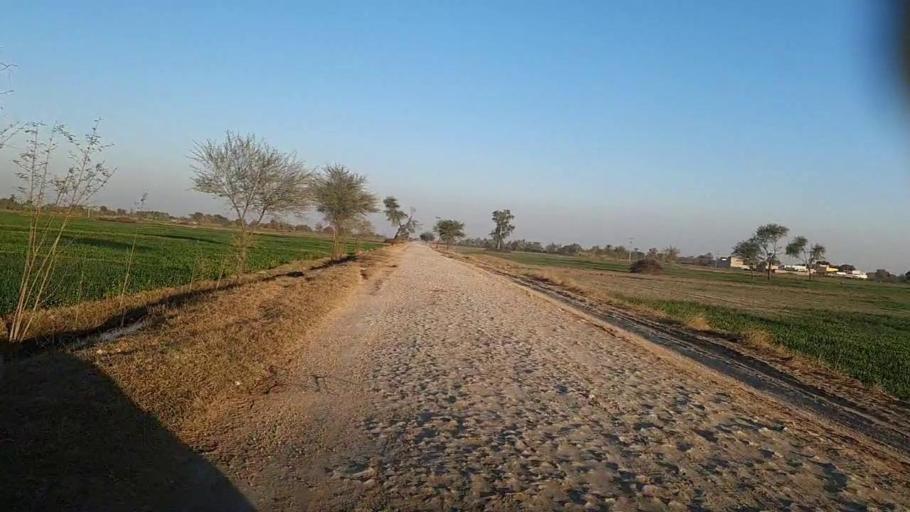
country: PK
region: Sindh
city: Khairpur
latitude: 27.9159
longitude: 69.6844
